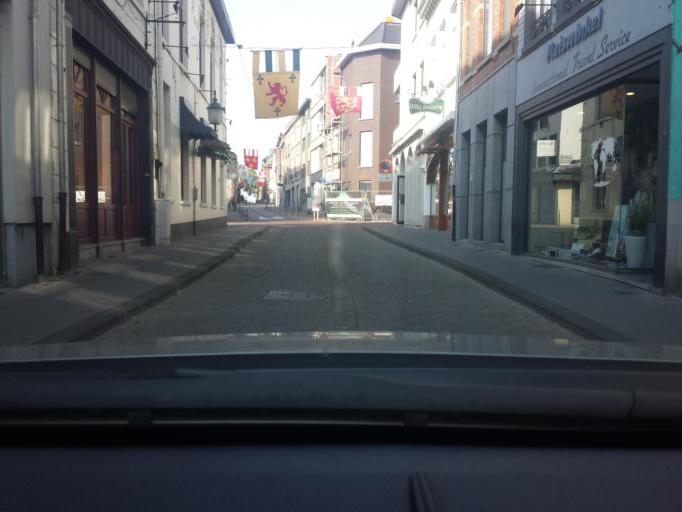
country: BE
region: Flanders
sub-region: Provincie Vlaams-Brabant
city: Diest
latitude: 50.9832
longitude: 5.0510
